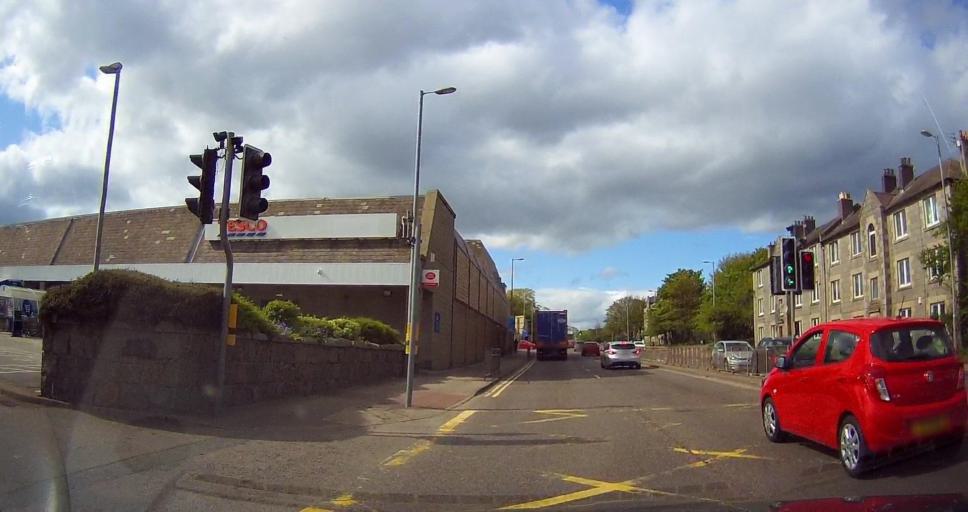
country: GB
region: Scotland
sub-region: Aberdeen City
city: Aberdeen
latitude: 57.1298
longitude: -2.0933
